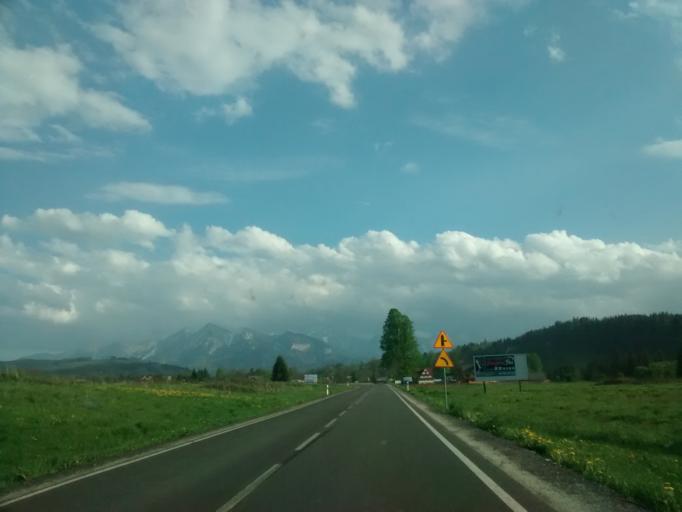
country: PL
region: Lesser Poland Voivodeship
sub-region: Powiat tatrzanski
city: Bukowina Tatrzanska
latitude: 49.3486
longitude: 20.1349
